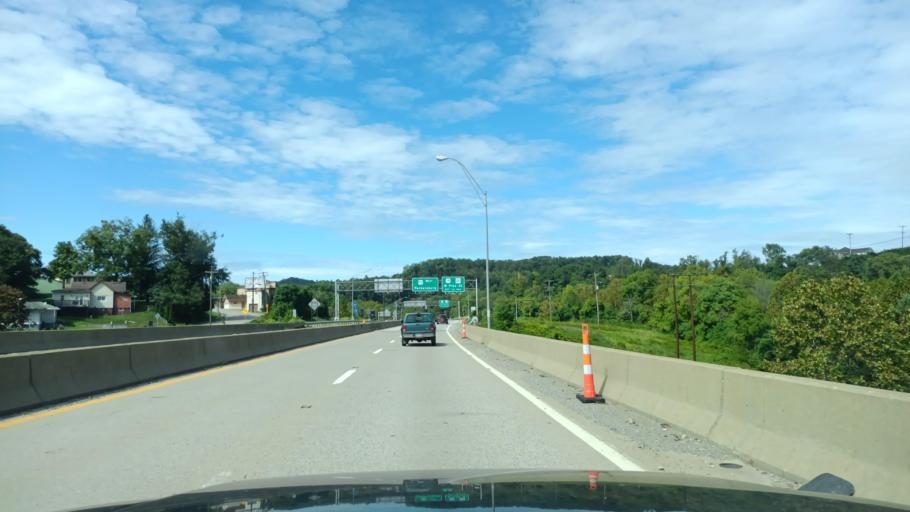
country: US
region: West Virginia
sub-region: Harrison County
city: Clarksburg
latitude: 39.2898
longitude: -80.3515
